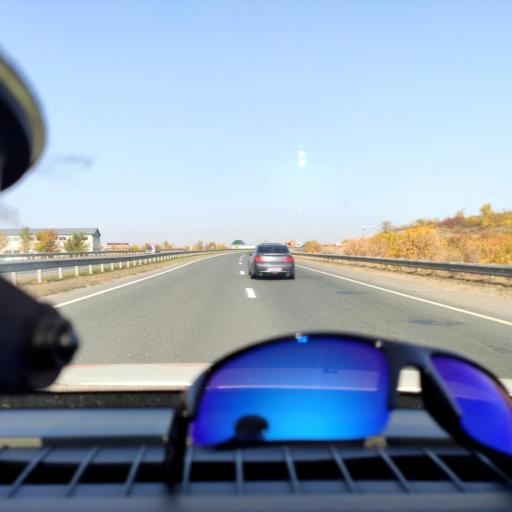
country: RU
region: Samara
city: Novokuybyshevsk
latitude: 53.0602
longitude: 50.0194
